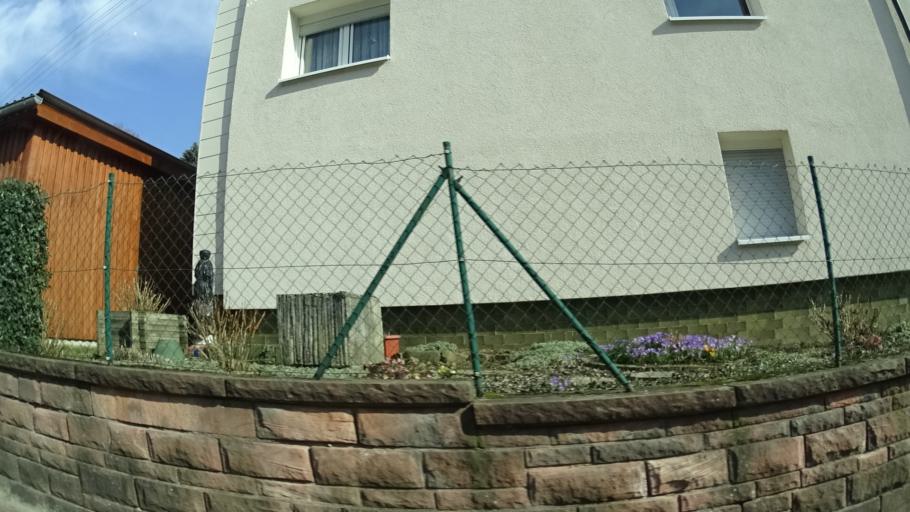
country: DE
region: Baden-Wuerttemberg
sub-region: Karlsruhe Region
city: Heiligkreuzsteinach
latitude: 49.4622
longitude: 8.8055
